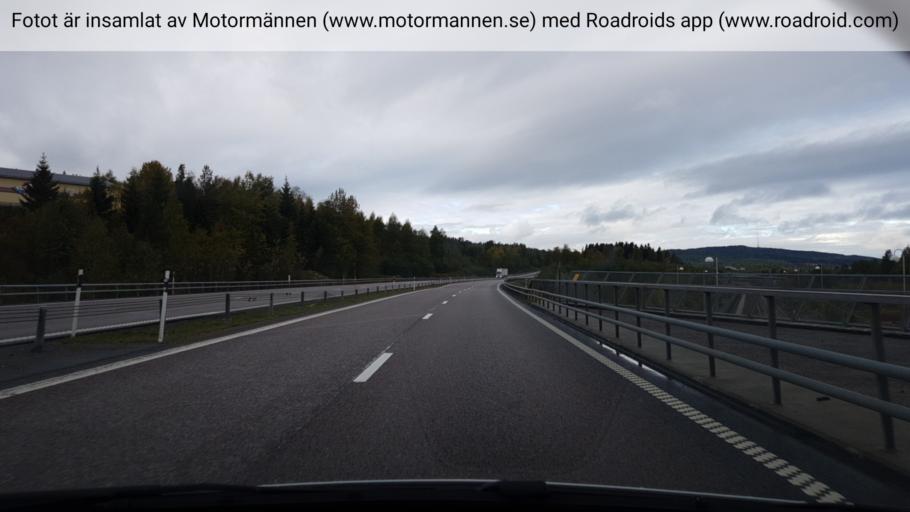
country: SE
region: Vaesternorrland
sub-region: OErnskoeldsviks Kommun
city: Ornskoldsvik
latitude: 63.3069
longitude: 18.7736
